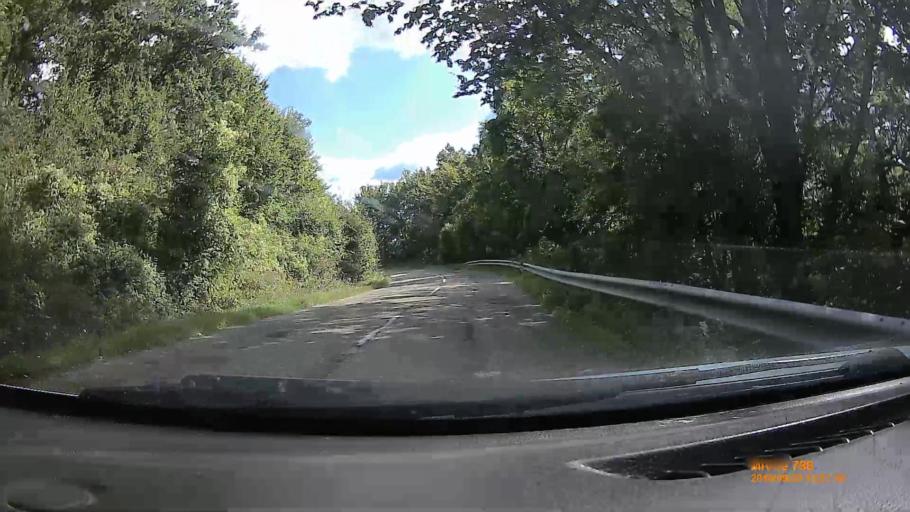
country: HU
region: Heves
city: Szilvasvarad
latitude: 48.0532
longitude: 20.4916
